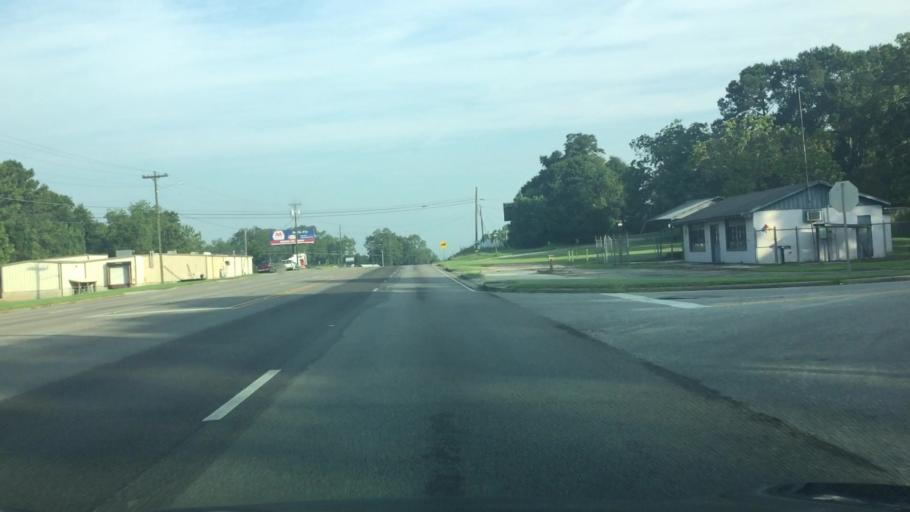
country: US
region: Alabama
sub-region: Covington County
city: Andalusia
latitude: 31.3236
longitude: -86.5067
